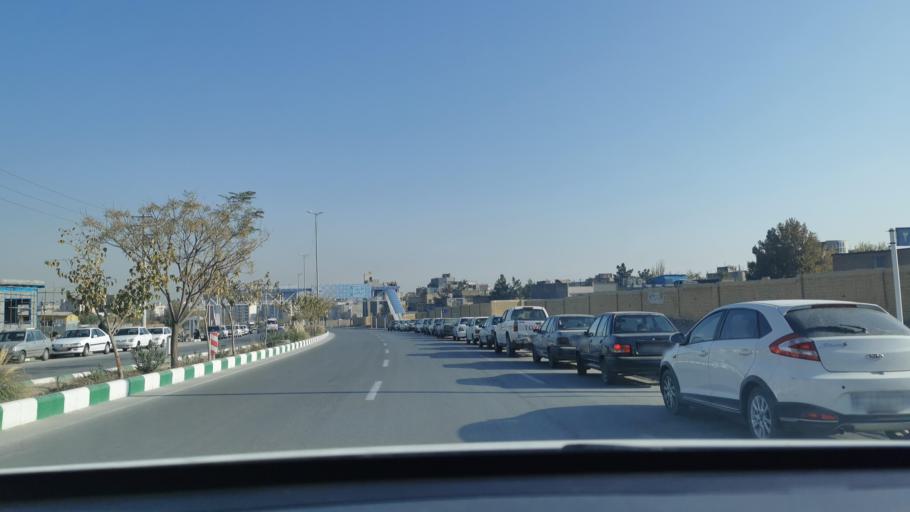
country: IR
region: Razavi Khorasan
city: Mashhad
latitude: 36.2767
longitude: 59.5398
